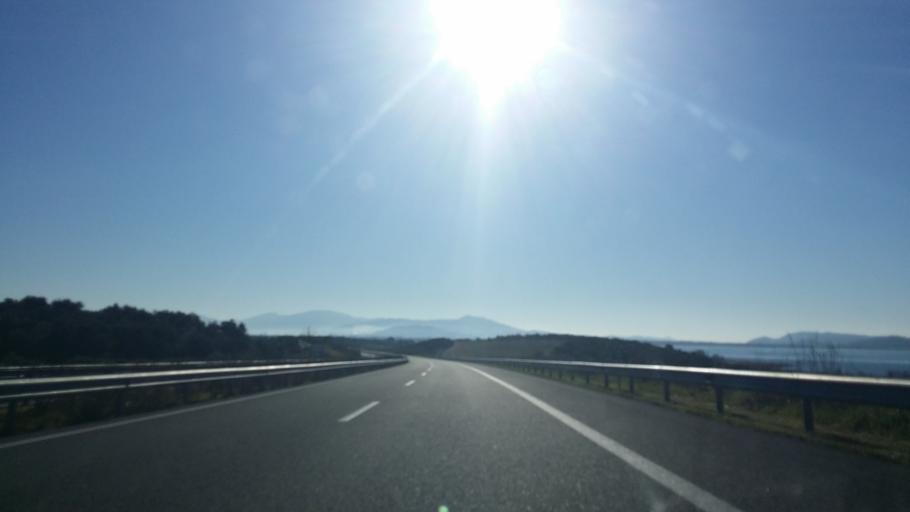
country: GR
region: West Greece
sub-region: Nomos Aitolias kai Akarnanias
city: Fitiai
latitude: 38.6799
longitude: 21.2192
